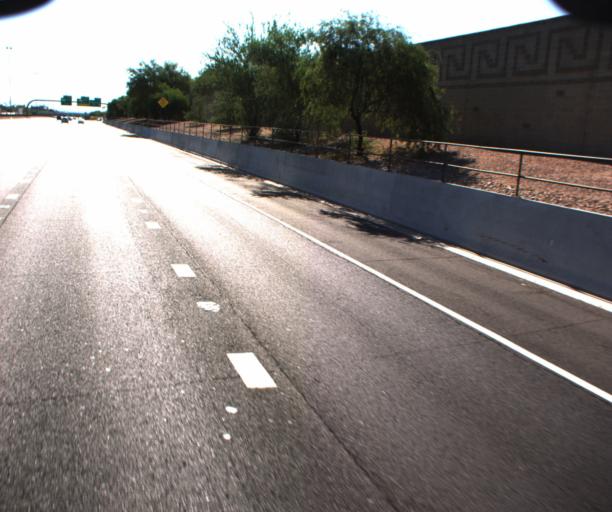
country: US
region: Arizona
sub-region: Maricopa County
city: Tempe
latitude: 33.3855
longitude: -111.9181
